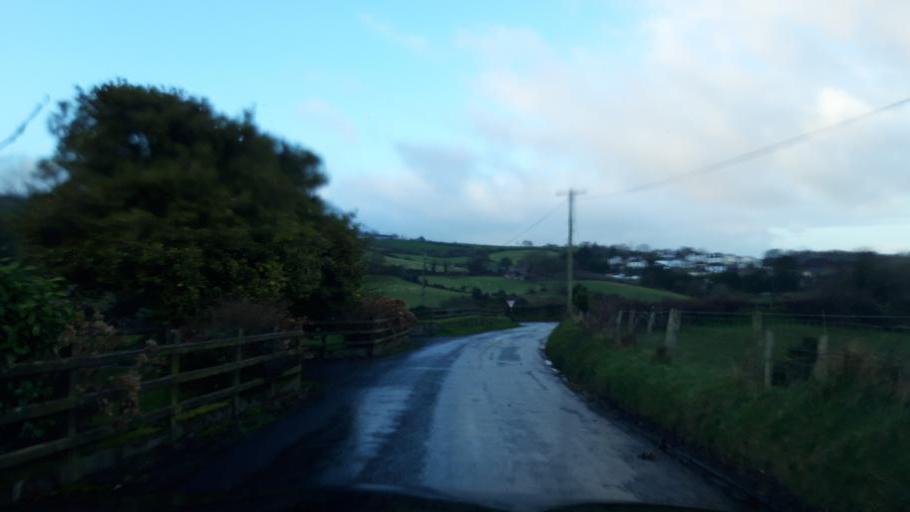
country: GB
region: Northern Ireland
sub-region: Moyle District
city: Ballycastle
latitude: 55.1965
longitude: -6.2256
